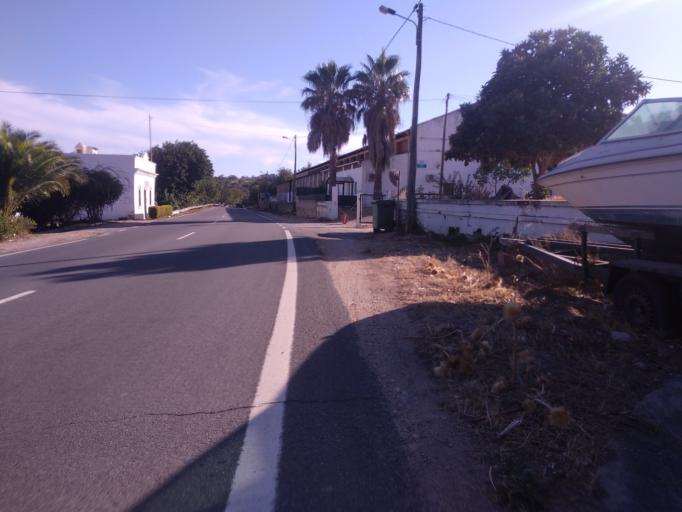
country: PT
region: Faro
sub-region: Sao Bras de Alportel
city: Sao Bras de Alportel
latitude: 37.1133
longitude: -7.9082
